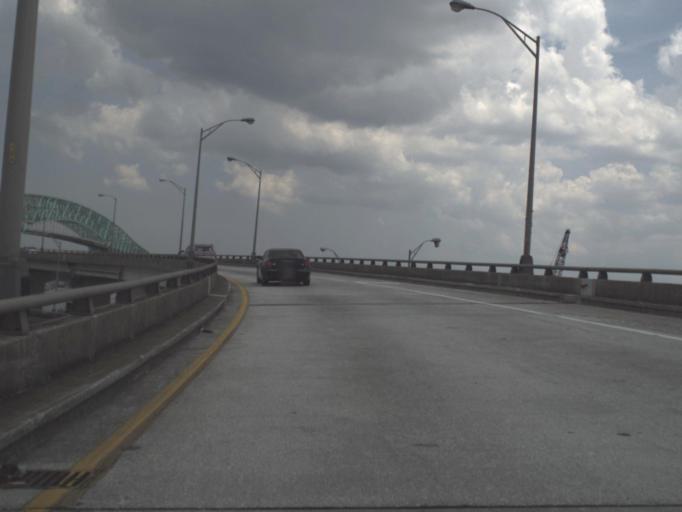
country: US
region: Florida
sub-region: Duval County
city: Jacksonville
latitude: 30.3213
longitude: -81.6345
